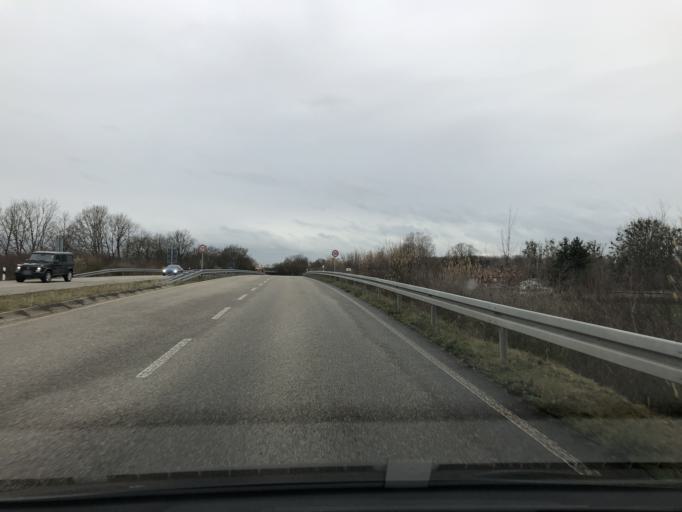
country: DE
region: Baden-Wuerttemberg
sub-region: Karlsruhe Region
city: Weingarten
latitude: 49.0106
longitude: 8.4740
